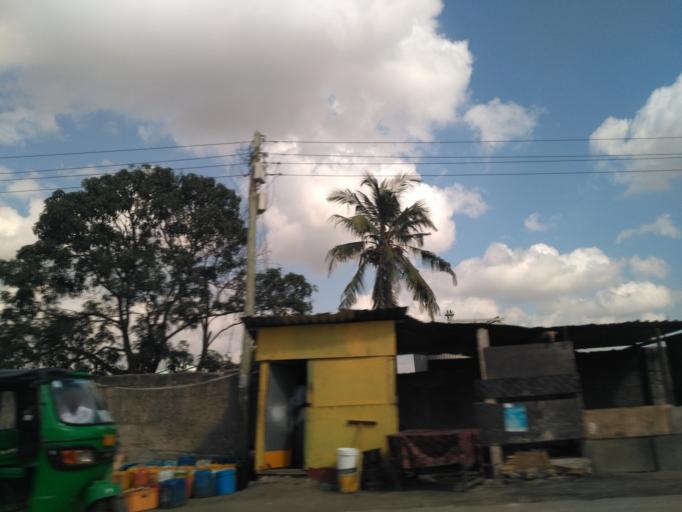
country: TZ
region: Dar es Salaam
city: Magomeni
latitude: -6.7612
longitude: 39.2382
